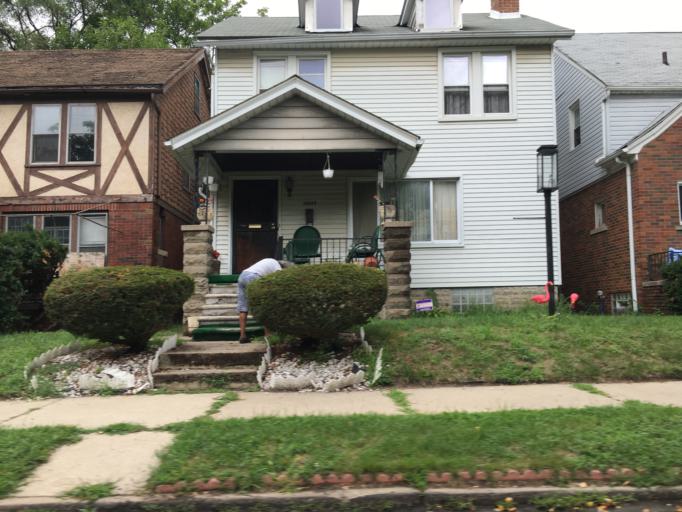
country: US
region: Michigan
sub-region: Oakland County
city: Ferndale
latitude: 42.4151
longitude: -83.1429
